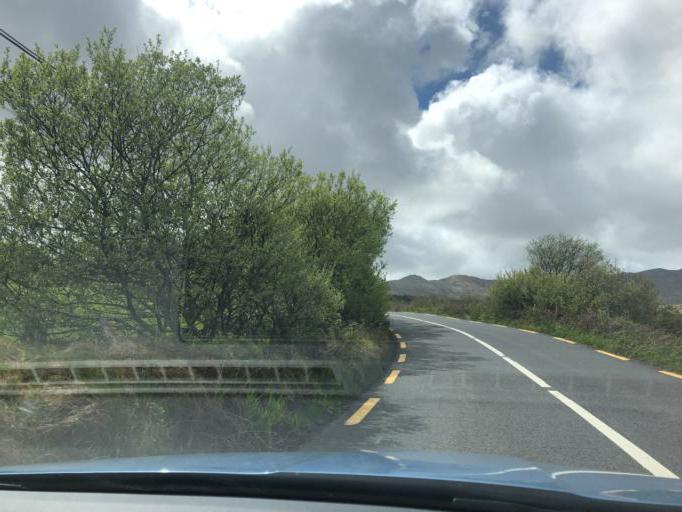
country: IE
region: Munster
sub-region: Ciarrai
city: Cahersiveen
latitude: 51.8302
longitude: -9.9451
